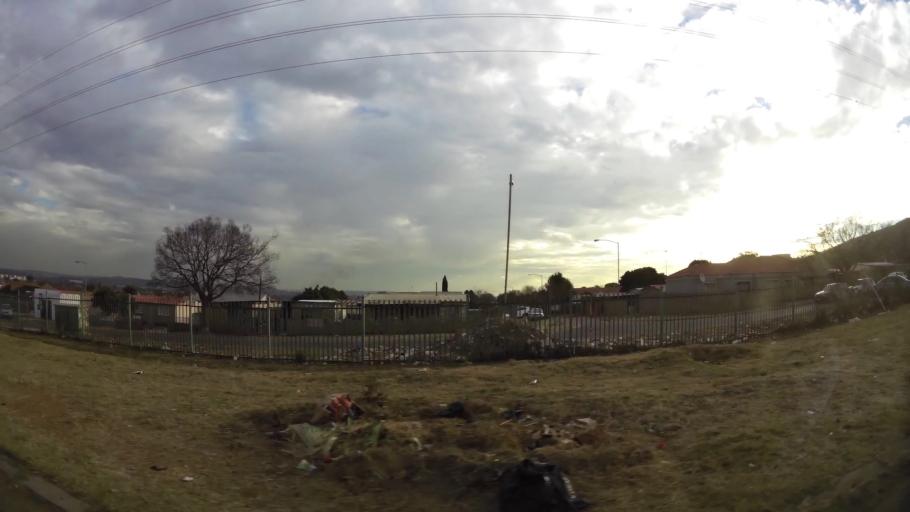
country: ZA
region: Gauteng
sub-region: City of Tshwane Metropolitan Municipality
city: Pretoria
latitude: -25.7016
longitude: 28.3231
